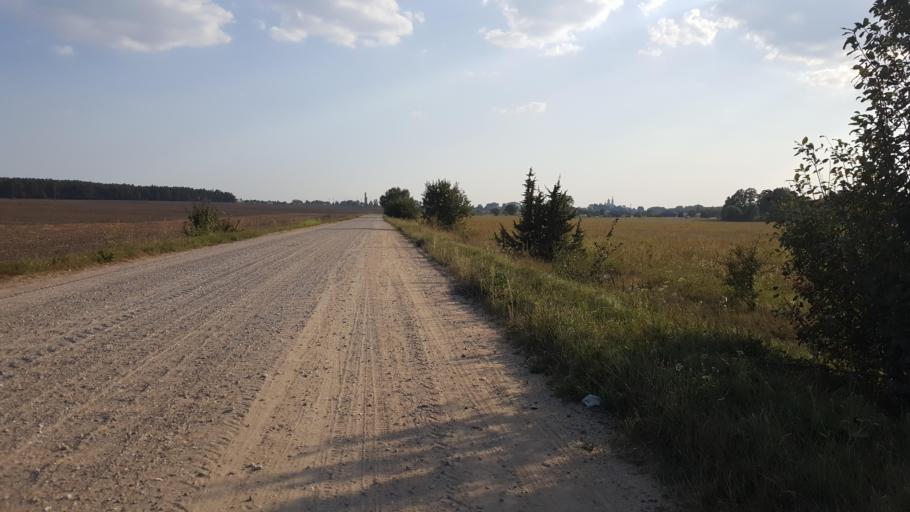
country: BY
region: Brest
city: Kamyanyets
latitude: 52.4175
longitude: 23.8411
